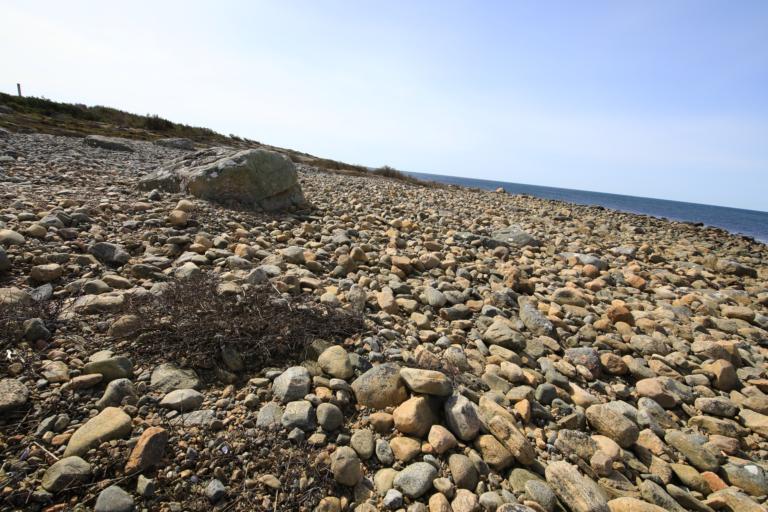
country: SE
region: Halland
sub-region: Kungsbacka Kommun
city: Frillesas
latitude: 57.2731
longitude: 12.1136
